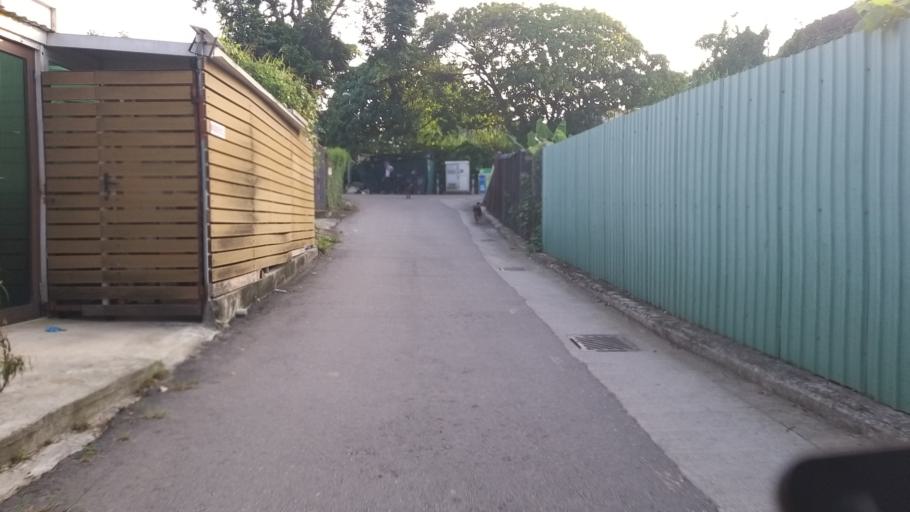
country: HK
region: Yuen Long
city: Yuen Long Kau Hui
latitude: 22.4492
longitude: 114.0150
